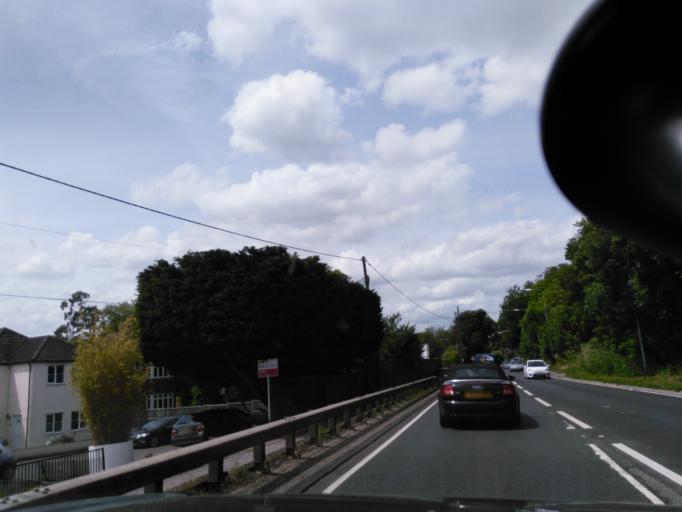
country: GB
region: England
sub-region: Wiltshire
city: Alderbury
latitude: 51.0596
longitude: -1.7620
